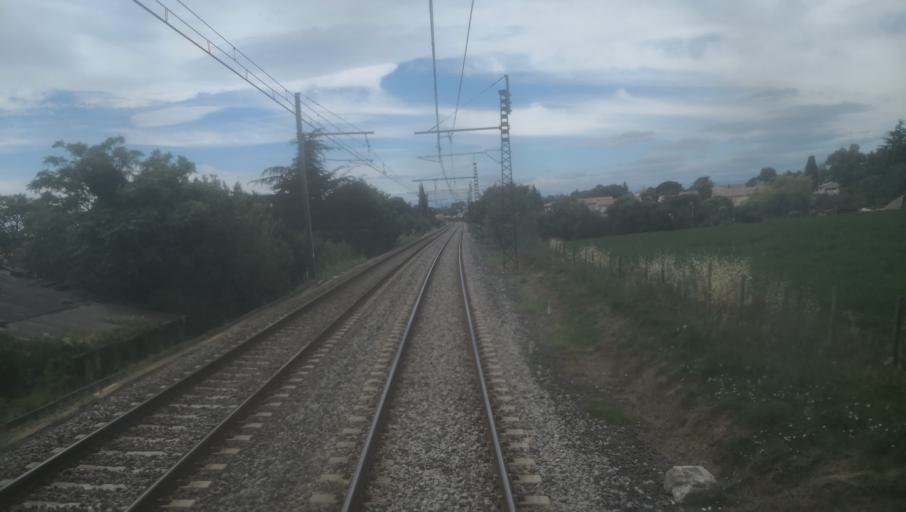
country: FR
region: Languedoc-Roussillon
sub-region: Departement de l'Herault
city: Cers
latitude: 43.3231
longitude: 3.3102
